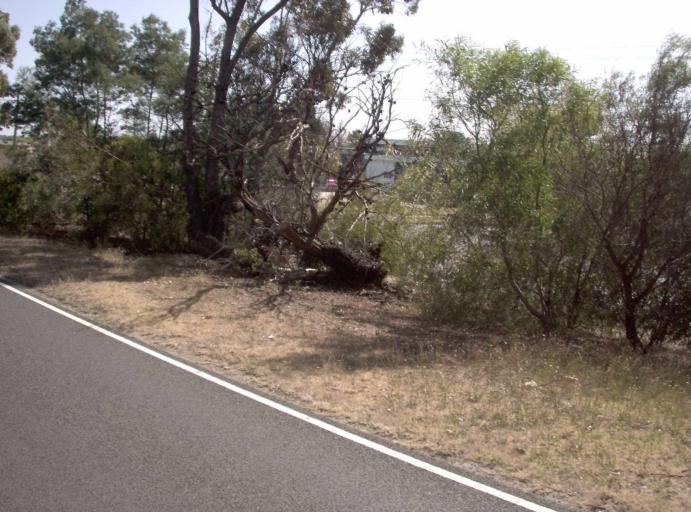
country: AU
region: Victoria
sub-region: Frankston
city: Carrum Downs
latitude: -38.1010
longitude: 145.1716
